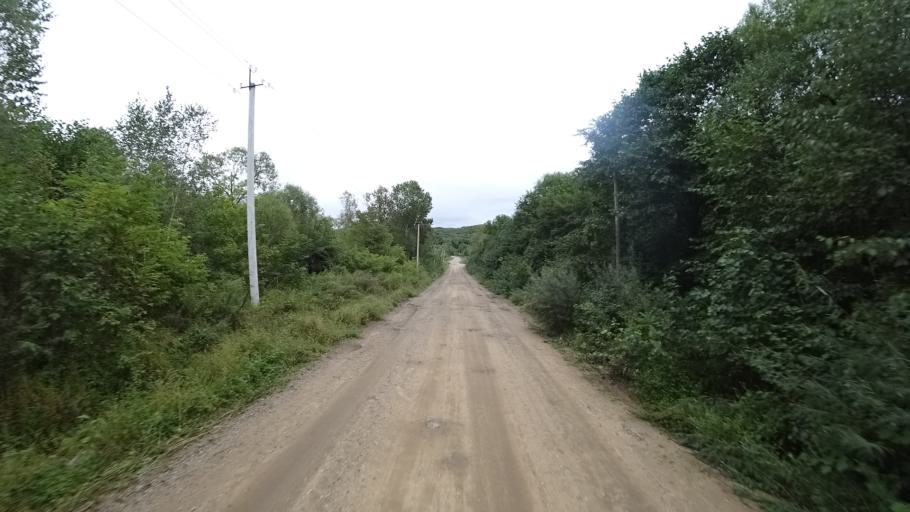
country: RU
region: Primorskiy
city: Rettikhovka
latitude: 44.1693
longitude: 132.7846
